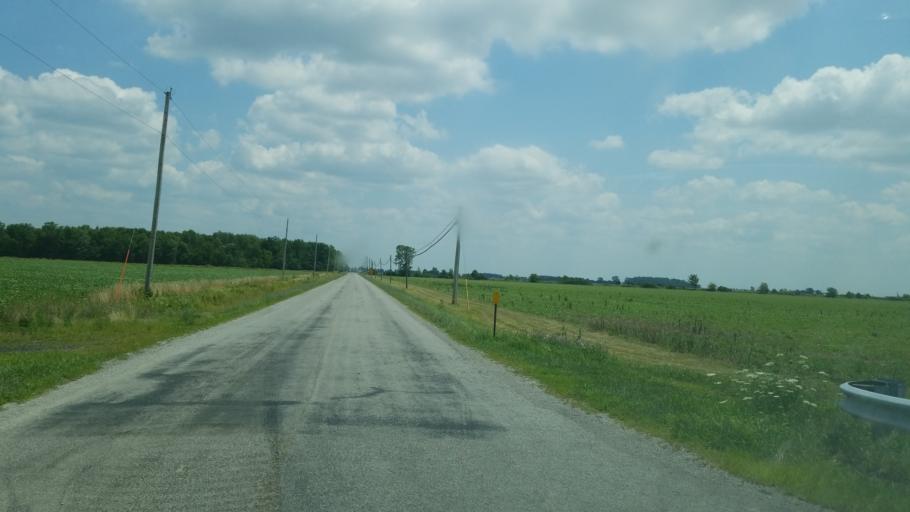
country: US
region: Ohio
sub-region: Henry County
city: Napoleon
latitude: 41.3417
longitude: -84.0380
